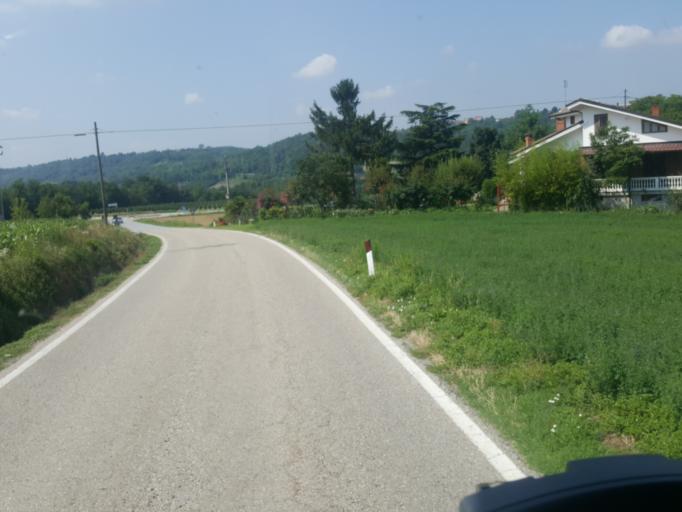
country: IT
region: Piedmont
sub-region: Provincia di Cuneo
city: Narzole
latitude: 44.6053
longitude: 7.8913
